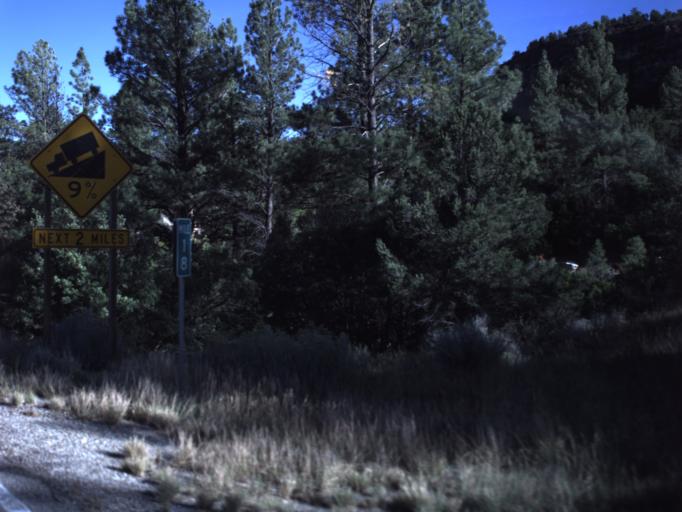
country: US
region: Utah
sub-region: Grand County
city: Moab
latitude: 38.3289
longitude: -109.1143
